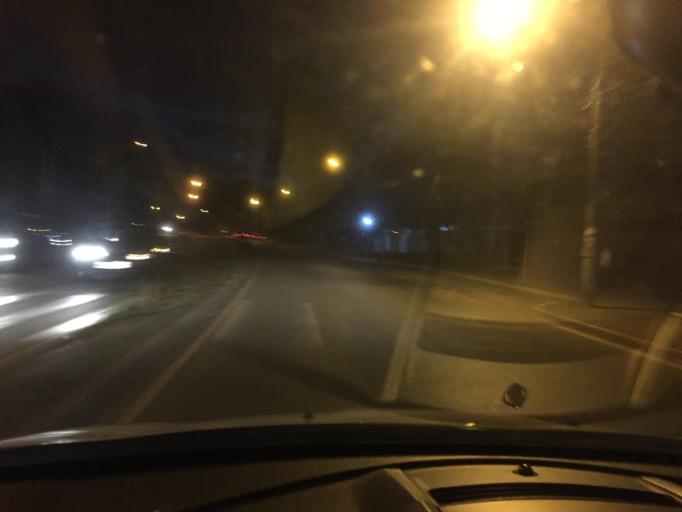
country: BR
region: Sao Paulo
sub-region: Varzea Paulista
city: Varzea Paulista
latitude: -23.2074
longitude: -46.8143
